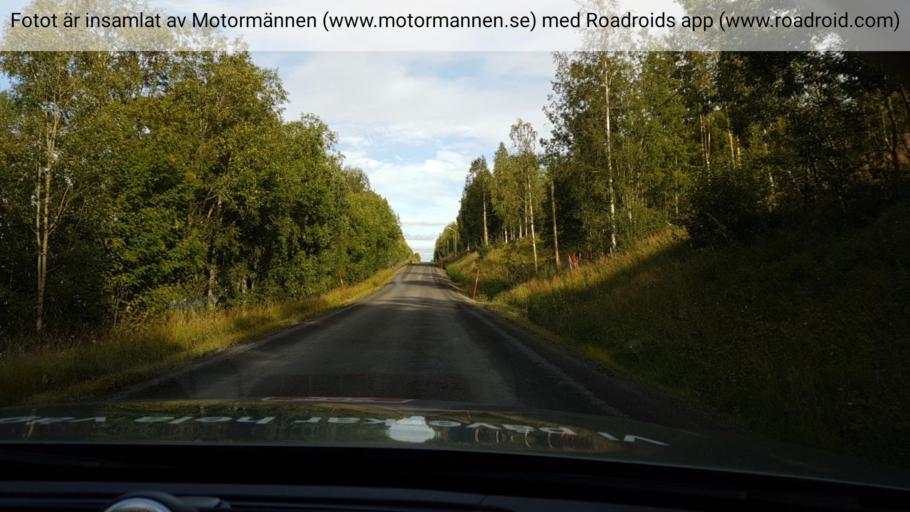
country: SE
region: Jaemtland
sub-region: Stroemsunds Kommun
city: Stroemsund
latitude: 64.1432
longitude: 15.7071
